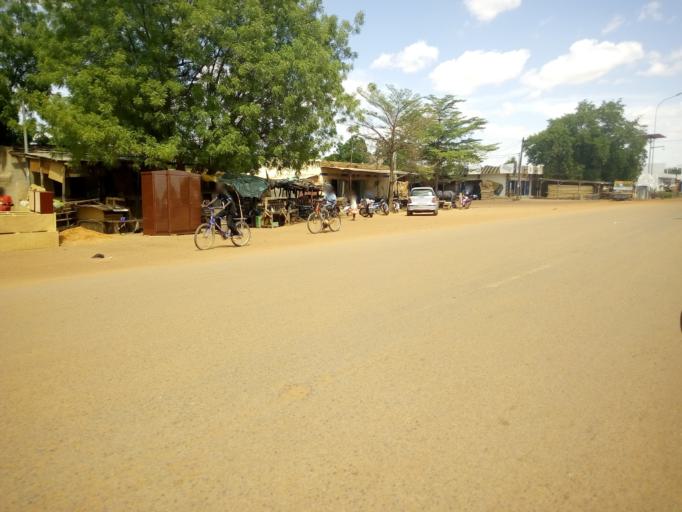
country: ML
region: Segou
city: Segou
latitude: 13.4353
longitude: -6.2644
